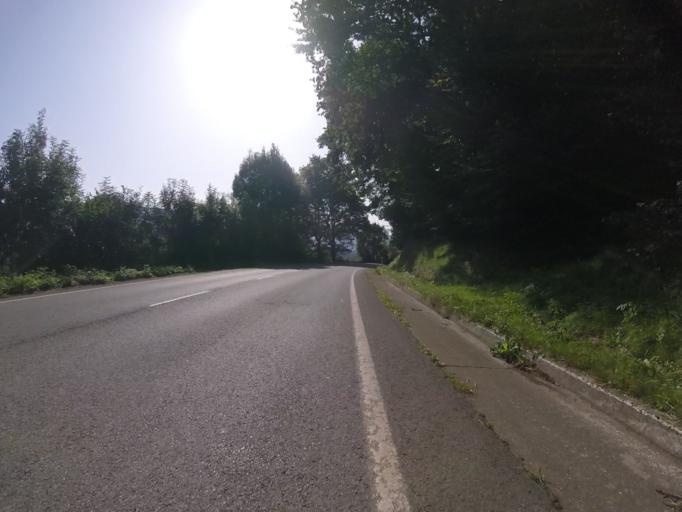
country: ES
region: Navarre
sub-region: Provincia de Navarra
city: Zugarramurdi
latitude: 43.2164
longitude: -1.4913
